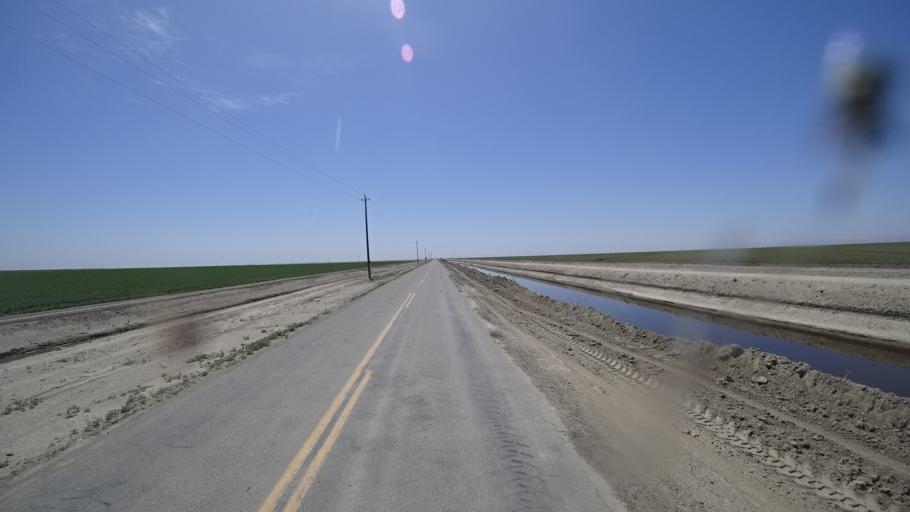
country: US
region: California
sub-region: Kings County
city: Corcoran
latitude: 36.1226
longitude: -119.6803
